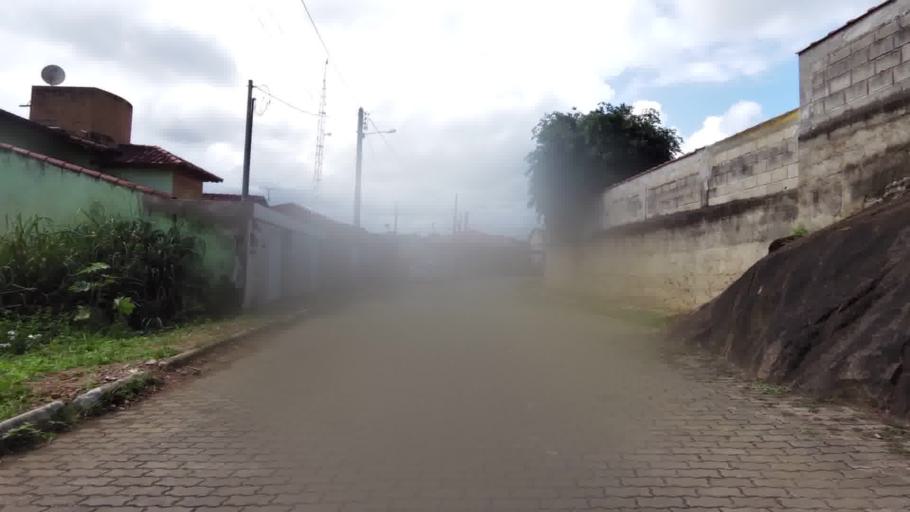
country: BR
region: Espirito Santo
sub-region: Piuma
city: Piuma
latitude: -20.8071
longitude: -40.6567
